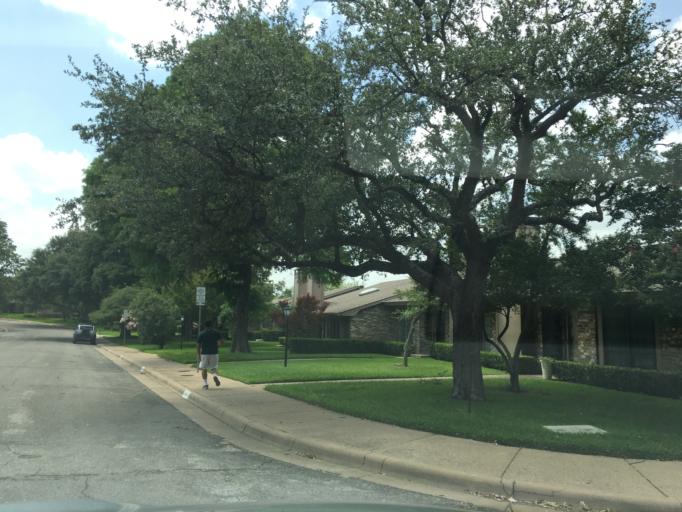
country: US
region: Texas
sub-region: Dallas County
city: University Park
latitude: 32.8931
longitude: -96.7750
